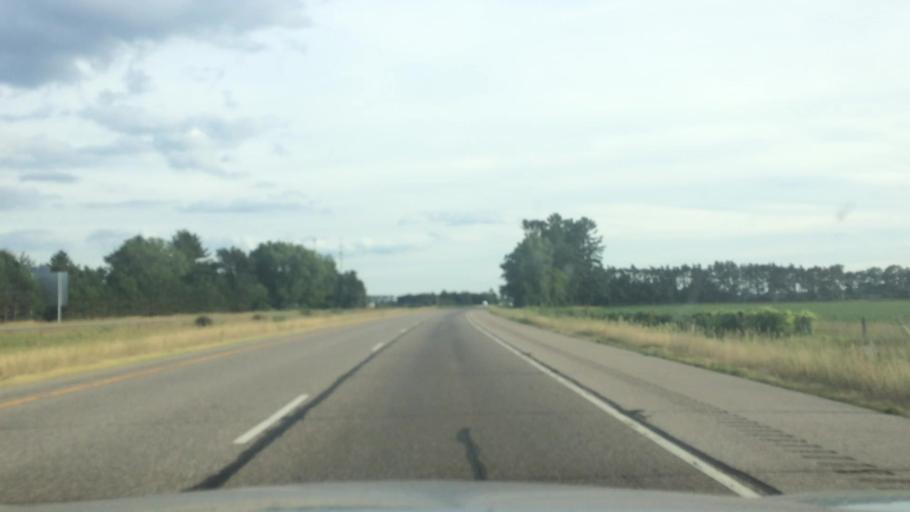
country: US
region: Wisconsin
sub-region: Portage County
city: Plover
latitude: 44.1952
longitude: -89.5233
